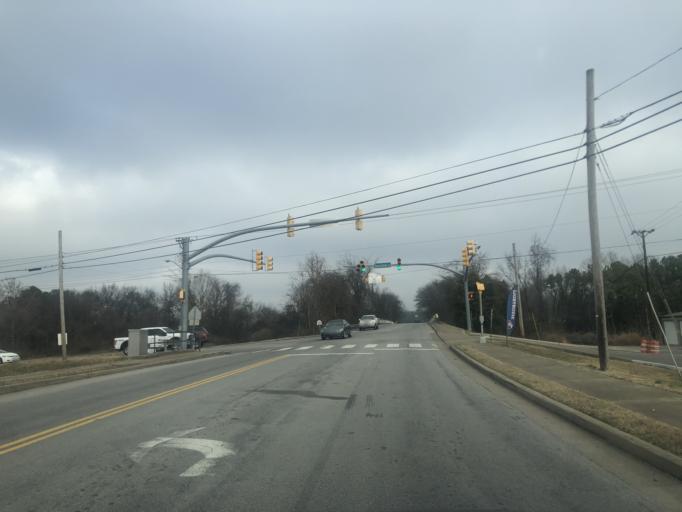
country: US
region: Tennessee
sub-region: Rutherford County
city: La Vergne
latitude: 36.0520
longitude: -86.6732
